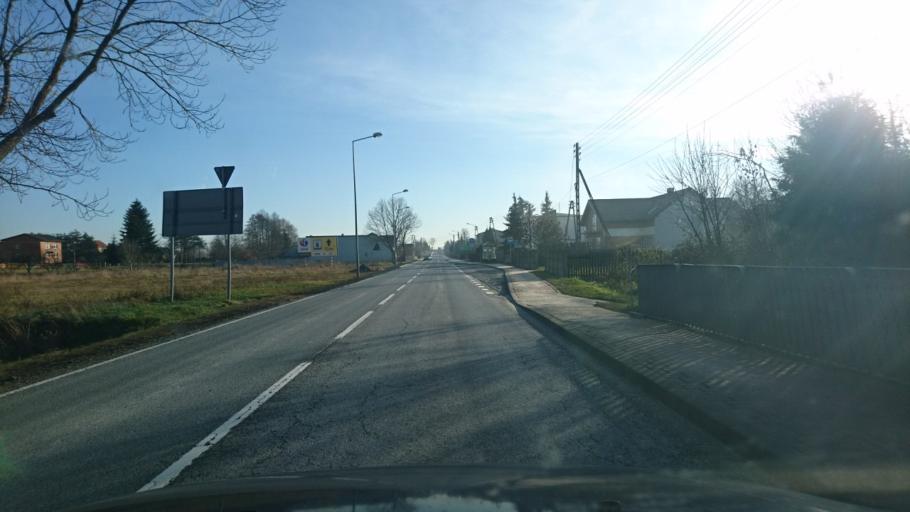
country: PL
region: Silesian Voivodeship
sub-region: Powiat klobucki
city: Starokrzepice
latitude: 51.0253
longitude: 18.6477
